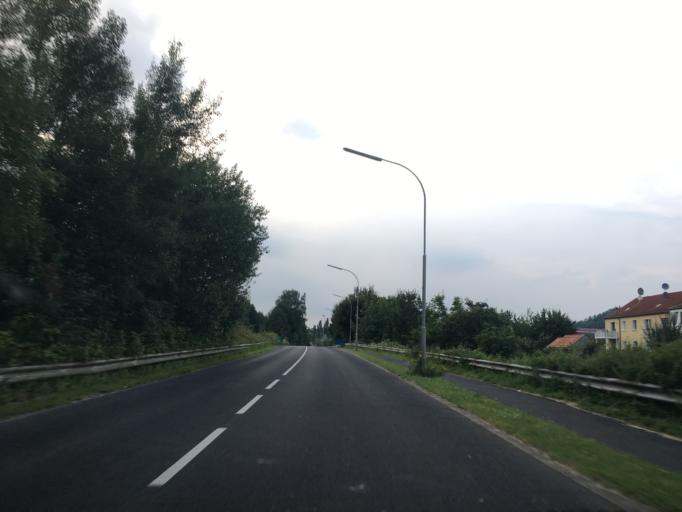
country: DE
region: North Rhine-Westphalia
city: Huckelhoven
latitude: 51.0710
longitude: 6.1901
